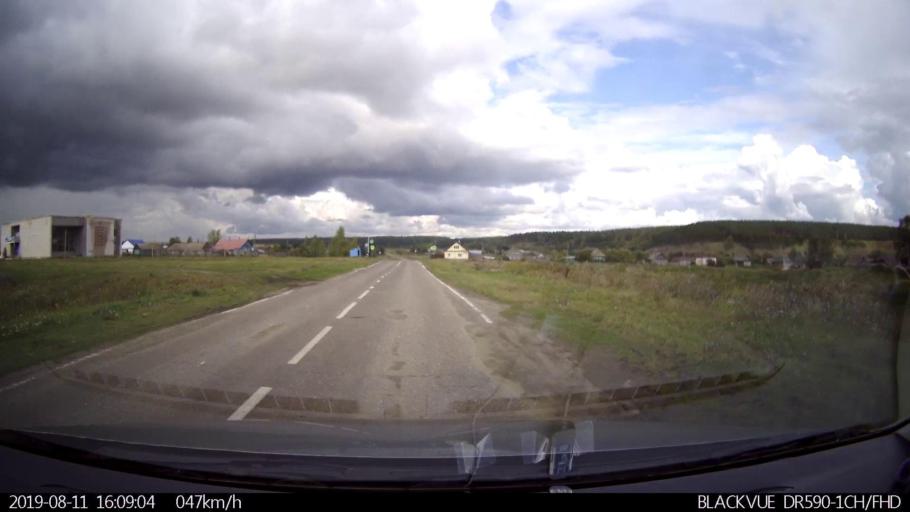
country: RU
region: Ulyanovsk
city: Ignatovka
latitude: 53.9895
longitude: 47.6509
